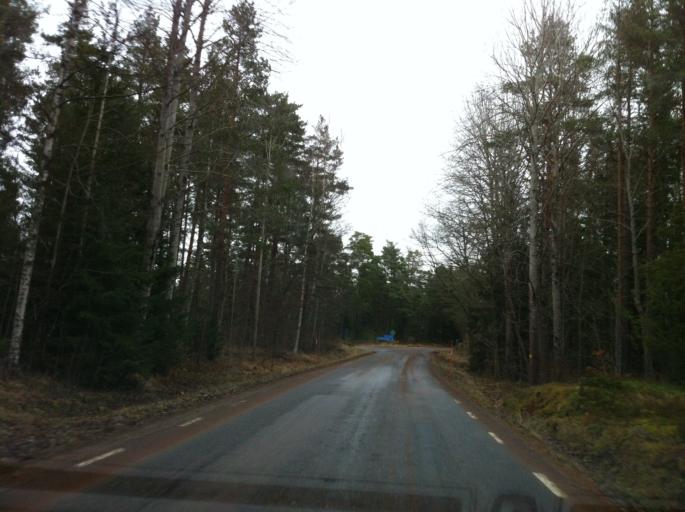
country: SE
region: Kalmar
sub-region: Vasterviks Kommun
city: Overum
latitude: 57.9027
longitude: 16.1021
